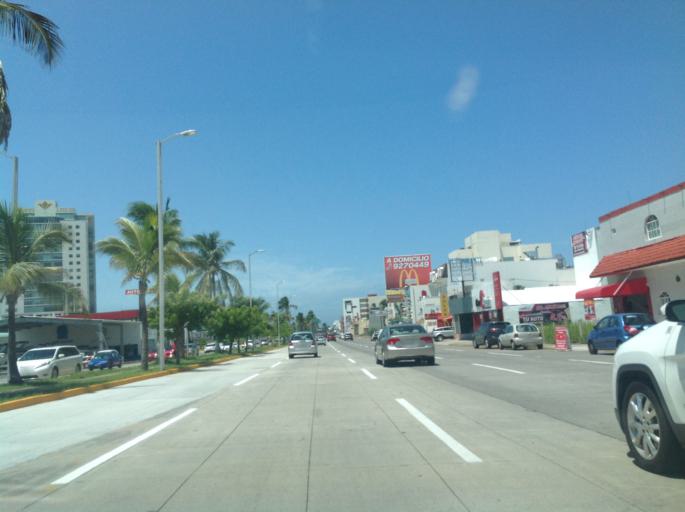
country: MX
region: Veracruz
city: Boca del Rio
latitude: 19.1438
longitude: -96.1038
